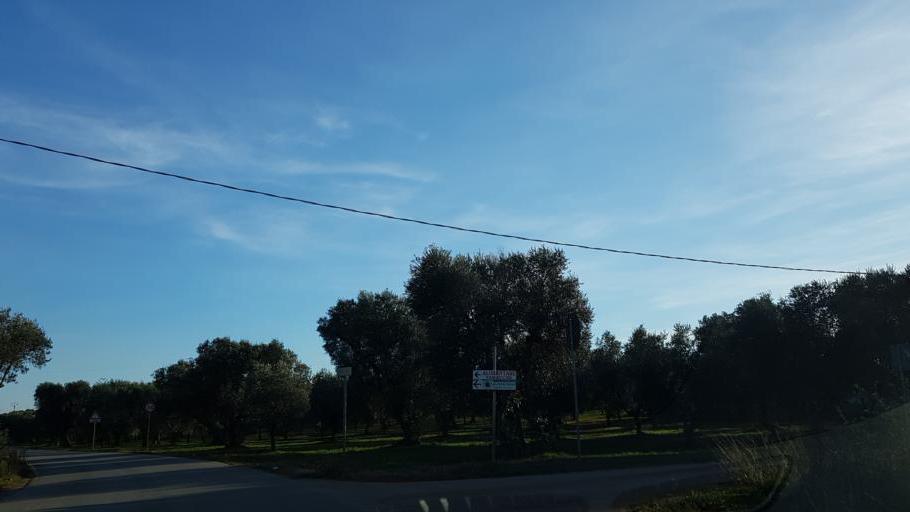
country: IT
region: Apulia
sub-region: Provincia di Brindisi
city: San Vito dei Normanni
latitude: 40.6918
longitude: 17.7621
